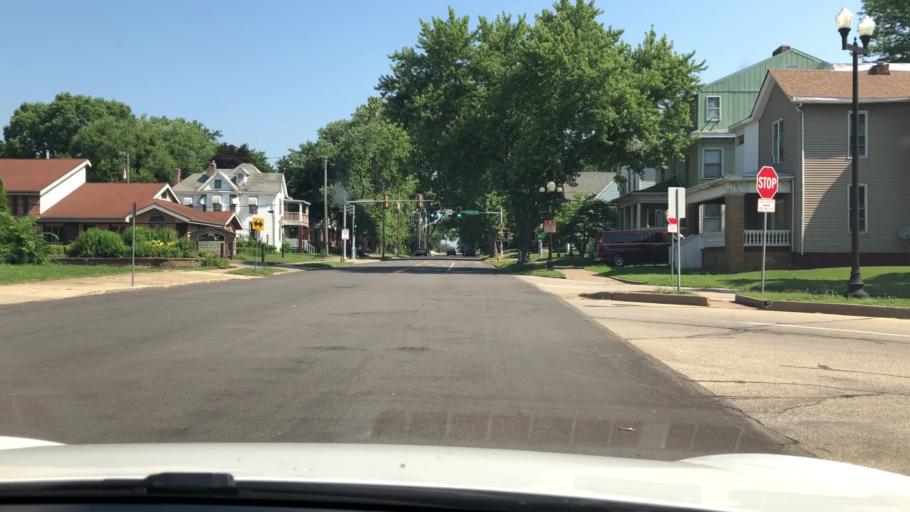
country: US
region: Illinois
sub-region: Peoria County
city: Peoria
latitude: 40.7024
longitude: -89.5988
